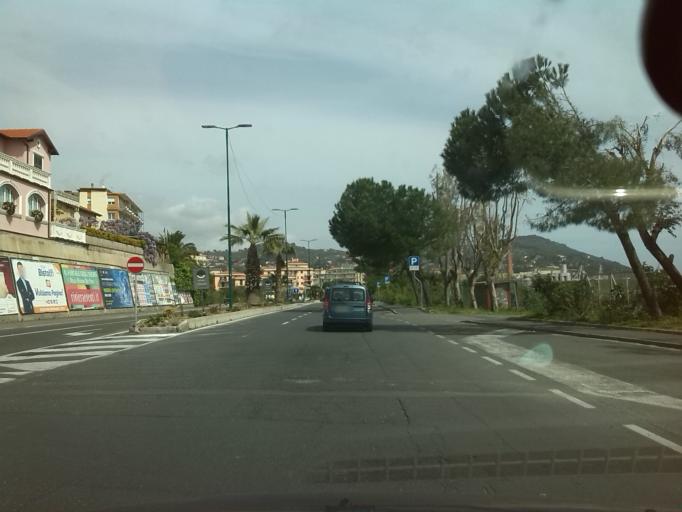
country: IT
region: Liguria
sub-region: Provincia di Imperia
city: Imperia
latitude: 43.8850
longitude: 8.0281
